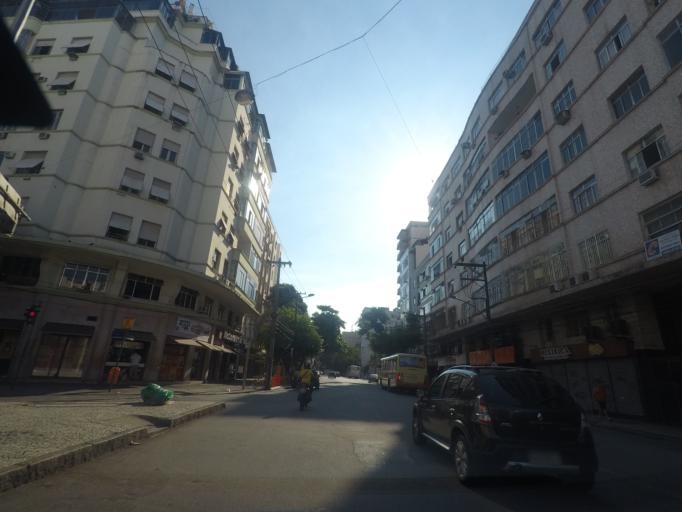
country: BR
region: Rio de Janeiro
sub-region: Rio De Janeiro
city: Rio de Janeiro
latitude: -22.9142
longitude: -43.2188
